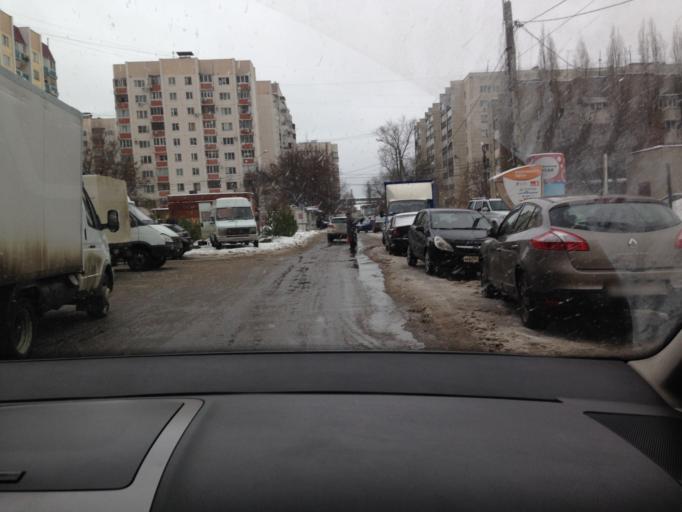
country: RU
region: Voronezj
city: Voronezh
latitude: 51.6706
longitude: 39.1842
